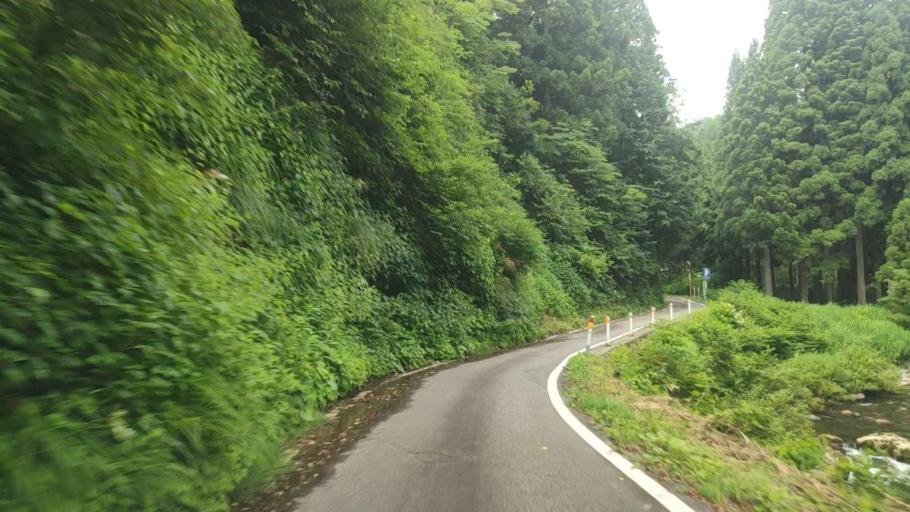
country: JP
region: Fukui
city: Katsuyama
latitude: 36.1904
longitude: 136.5249
